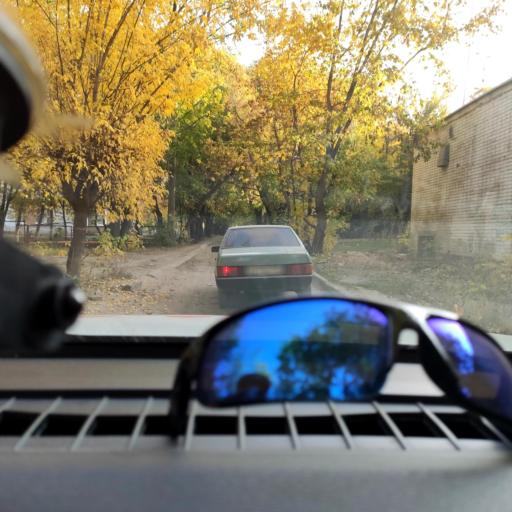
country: RU
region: Samara
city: Samara
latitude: 53.2159
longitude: 50.2072
